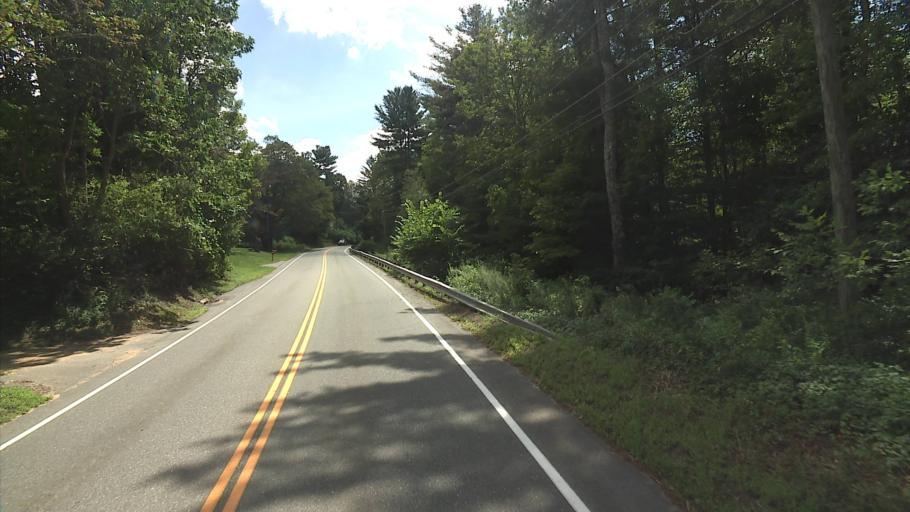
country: US
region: Connecticut
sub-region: Windham County
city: South Woodstock
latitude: 41.9446
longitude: -72.0760
